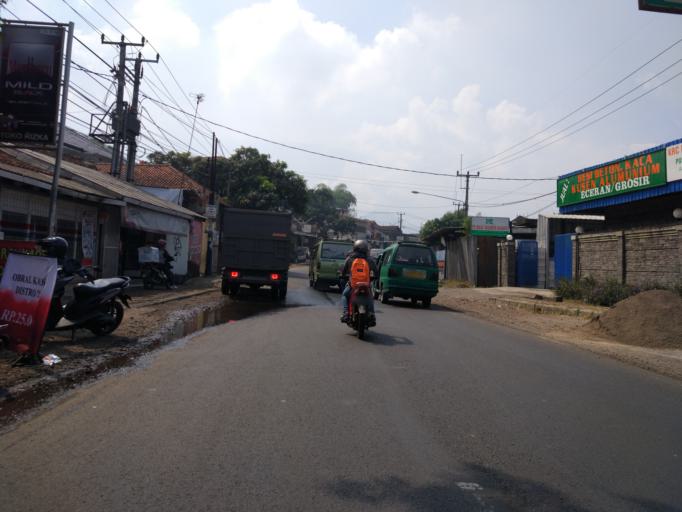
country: ID
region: West Java
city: Cileunyi
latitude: -6.9390
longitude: 107.7476
